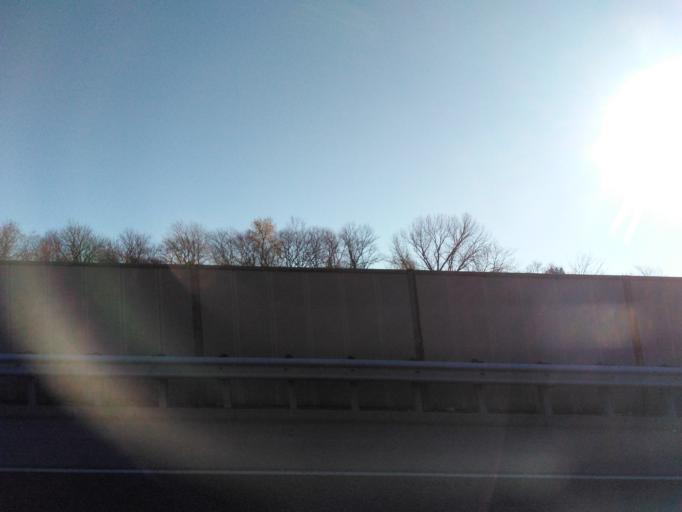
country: US
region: Illinois
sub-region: Saint Clair County
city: Caseyville
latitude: 38.6638
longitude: -90.0295
